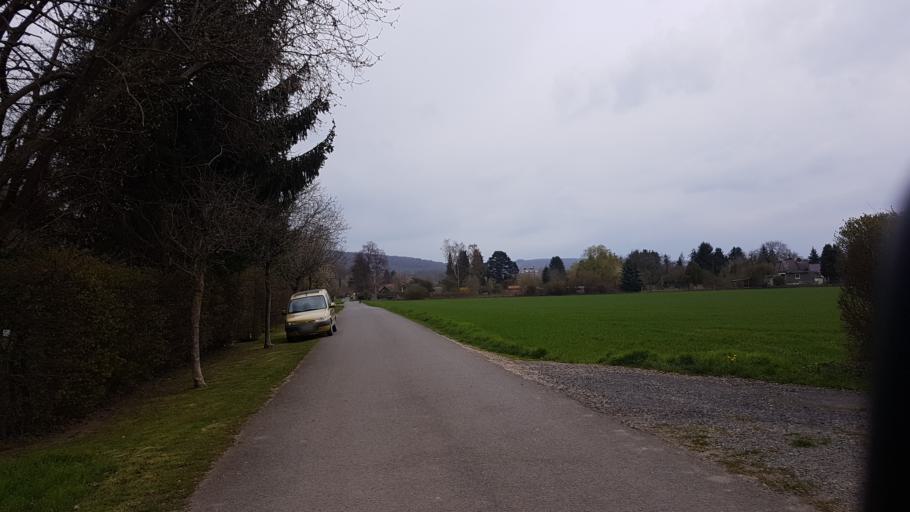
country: DE
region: Lower Saxony
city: Hameln
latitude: 52.1246
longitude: 9.3326
